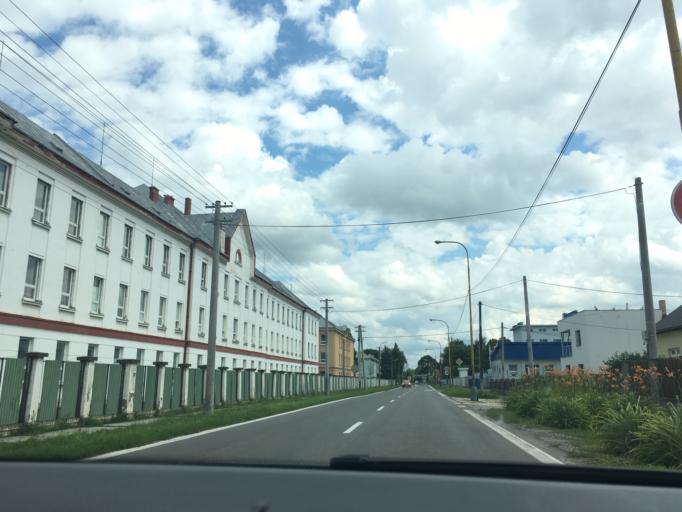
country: SK
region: Kosicky
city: Trebisov
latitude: 48.6358
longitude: 21.7112
